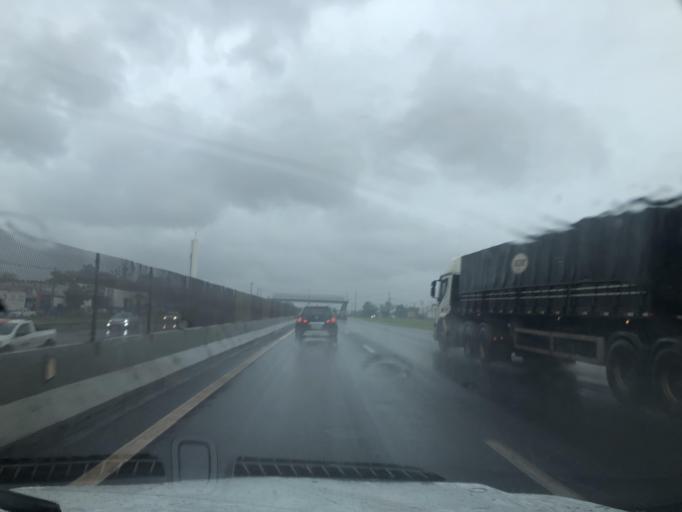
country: BR
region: Sao Paulo
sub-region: Ribeirao Preto
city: Ribeirao Preto
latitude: -21.1815
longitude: -47.7570
